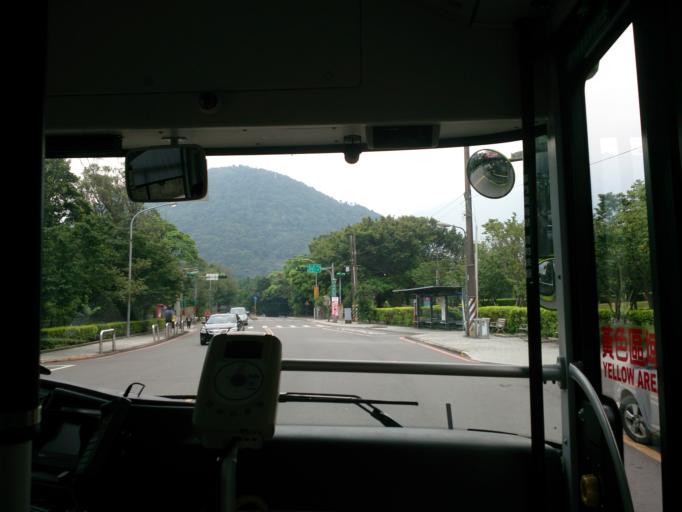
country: TW
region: Taipei
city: Taipei
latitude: 25.1384
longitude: 121.5465
